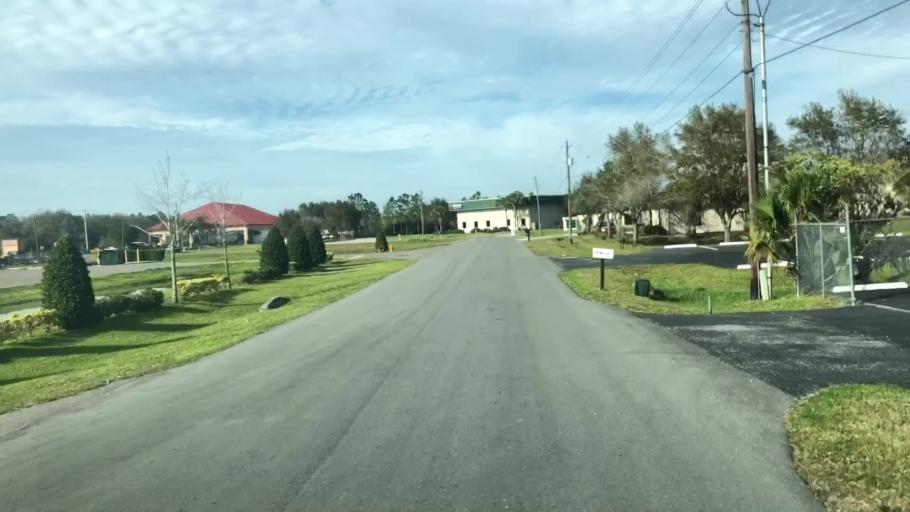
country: US
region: Florida
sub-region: Polk County
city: Winston
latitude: 27.9982
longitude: -82.0172
